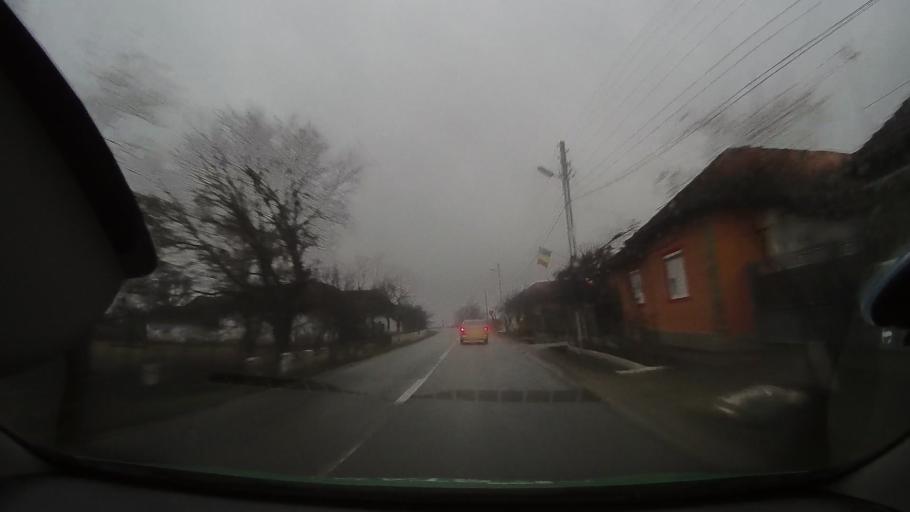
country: RO
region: Arad
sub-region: Comuna Craiova
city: Craiova
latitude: 46.5497
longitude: 21.9604
